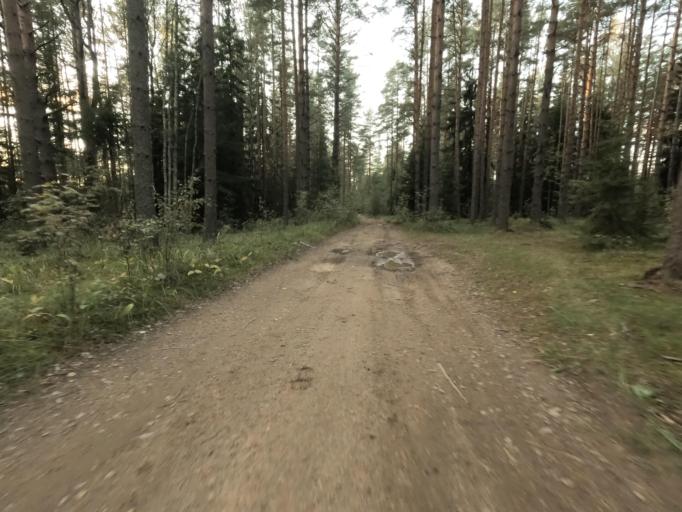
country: RU
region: Leningrad
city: Otradnoye
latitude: 59.8450
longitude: 30.8000
